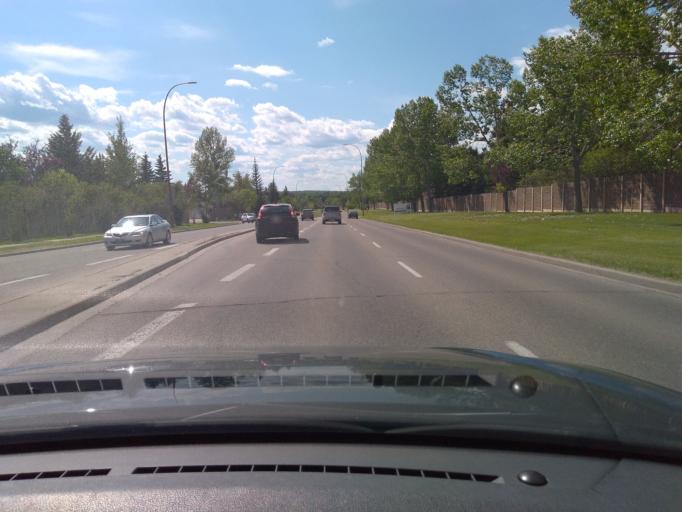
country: CA
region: Alberta
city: Calgary
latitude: 50.9722
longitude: -114.1126
